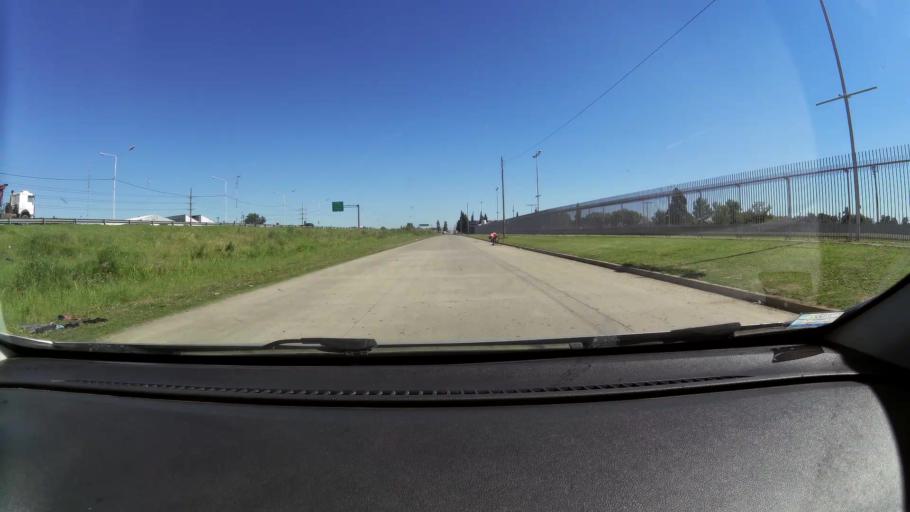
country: AR
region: Santa Fe
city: Perez
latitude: -32.9754
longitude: -60.7136
